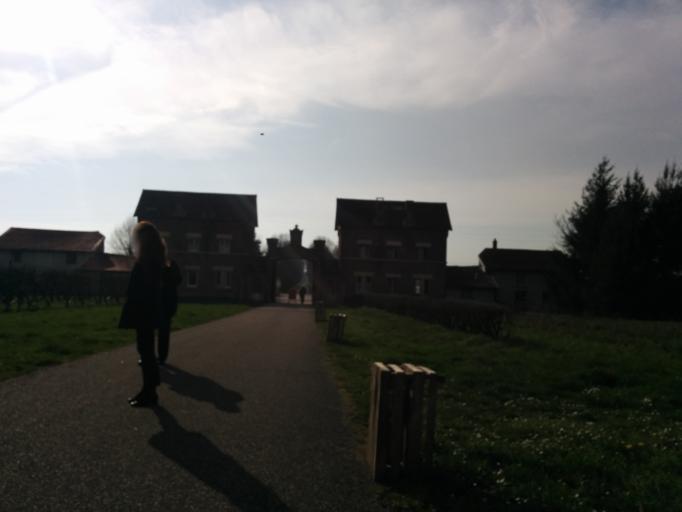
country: FR
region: Rhone-Alpes
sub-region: Departement de l'Ain
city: Saint-Paul-de-Varax
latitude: 46.0379
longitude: 5.0950
